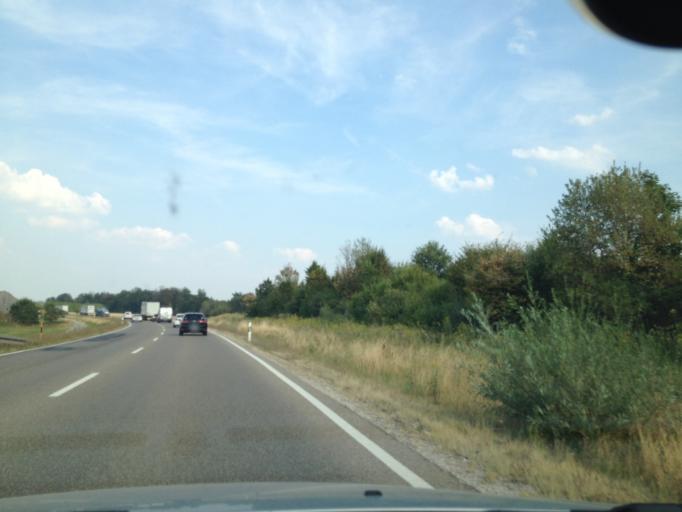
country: DE
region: Bavaria
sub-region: Swabia
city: Kaisheim
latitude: 48.7780
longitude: 10.7938
